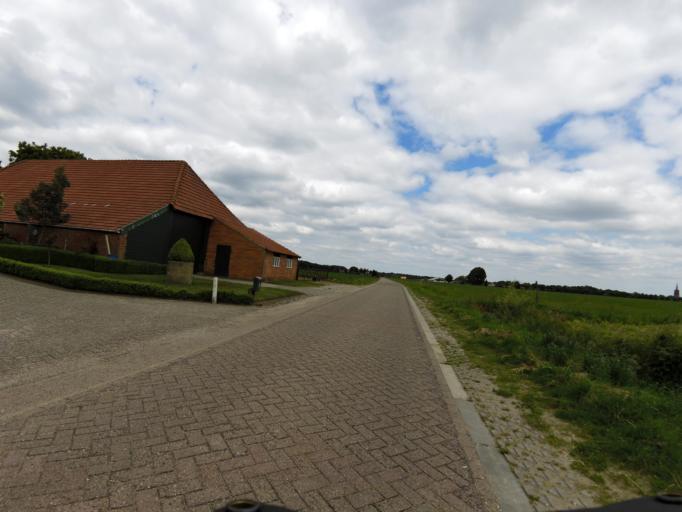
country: NL
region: North Brabant
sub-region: Gemeente Baarle-Nassau
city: Baarle-Nassau
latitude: 51.4769
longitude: 4.9399
